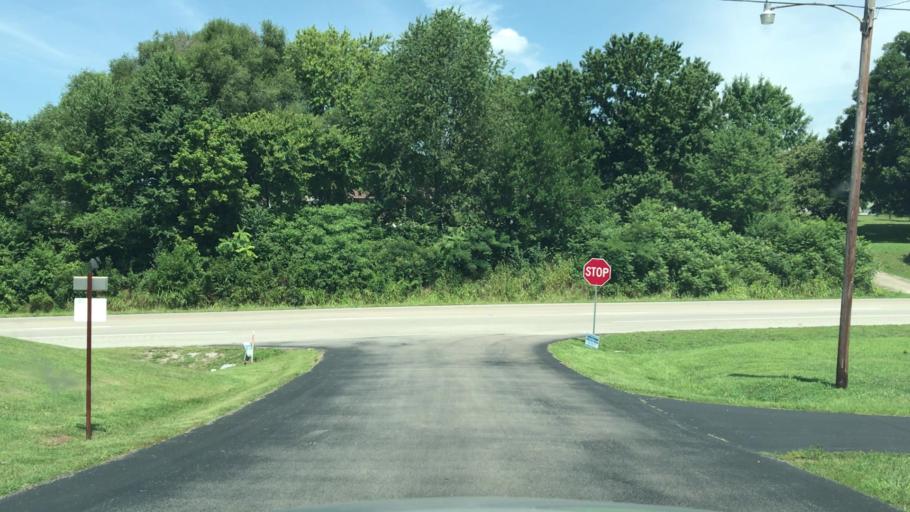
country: US
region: Kentucky
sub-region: Wayne County
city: Monticello
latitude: 36.8181
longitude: -84.8725
